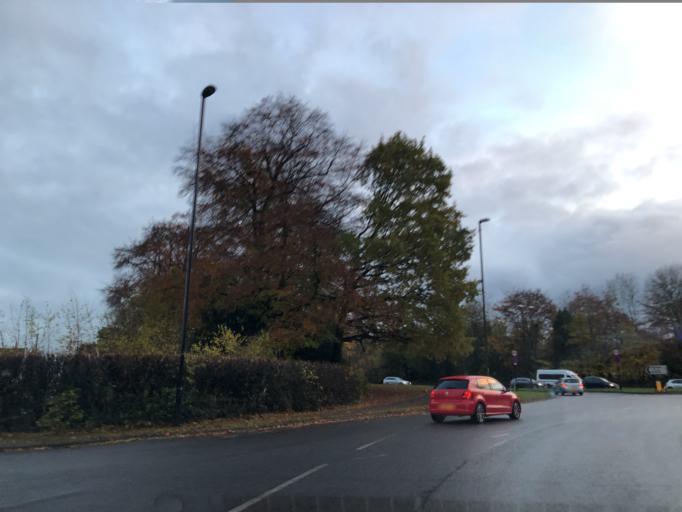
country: GB
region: England
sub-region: Coventry
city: Keresley
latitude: 52.4208
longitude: -1.5548
